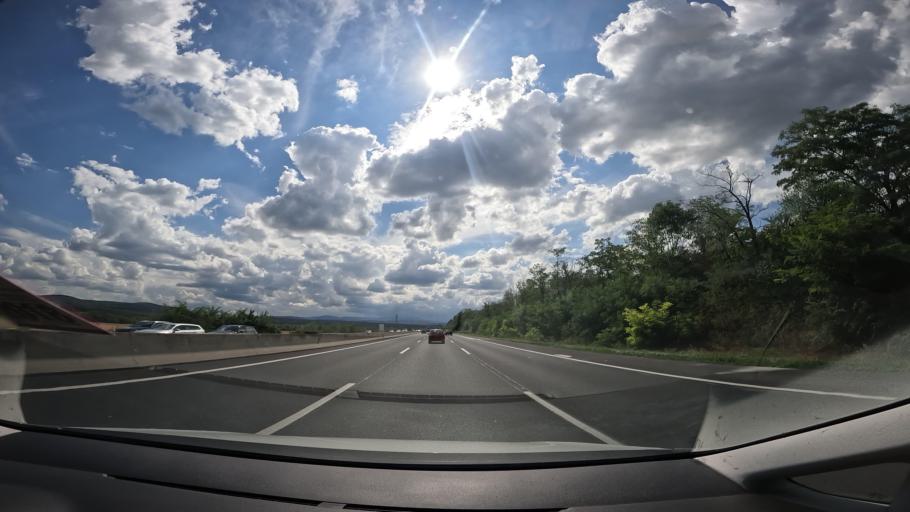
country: AT
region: Lower Austria
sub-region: Politischer Bezirk Neunkirchen
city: Breitenau
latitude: 47.7298
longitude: 16.1554
